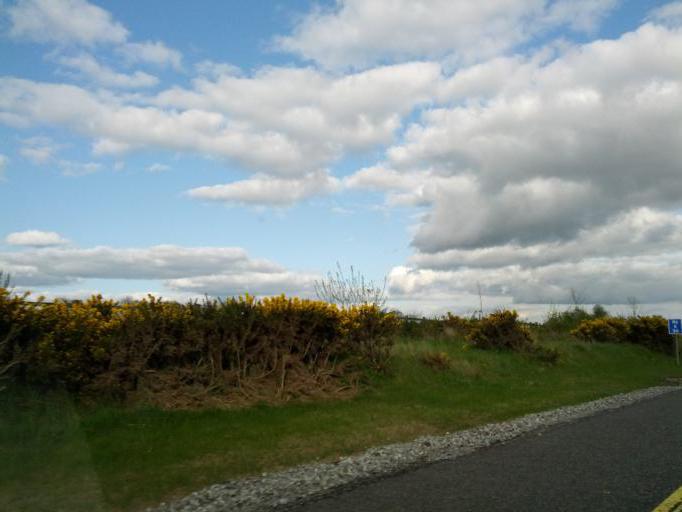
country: IE
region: Leinster
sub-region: An Iarmhi
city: Kilbeggan
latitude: 53.3746
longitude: -7.5502
